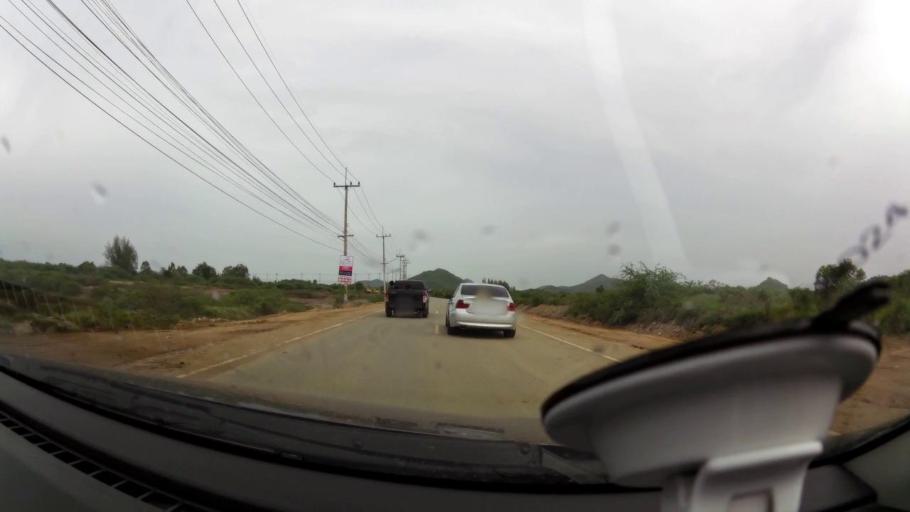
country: TH
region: Prachuap Khiri Khan
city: Pran Buri
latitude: 12.4030
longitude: 99.9679
